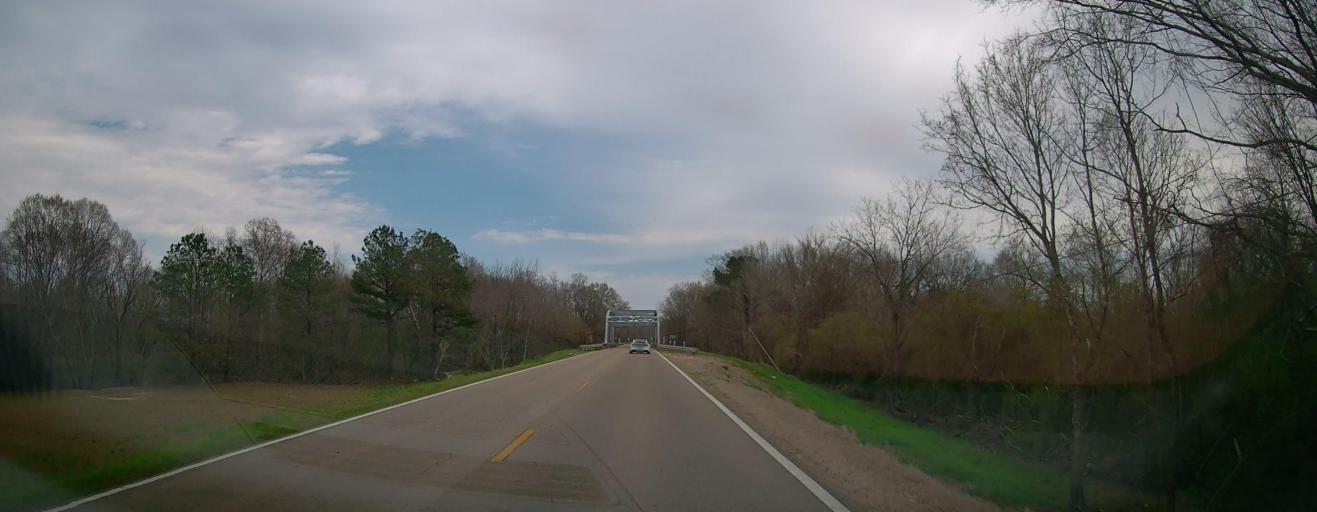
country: US
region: Mississippi
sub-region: Itawamba County
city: Fulton
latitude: 34.2528
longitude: -88.4780
